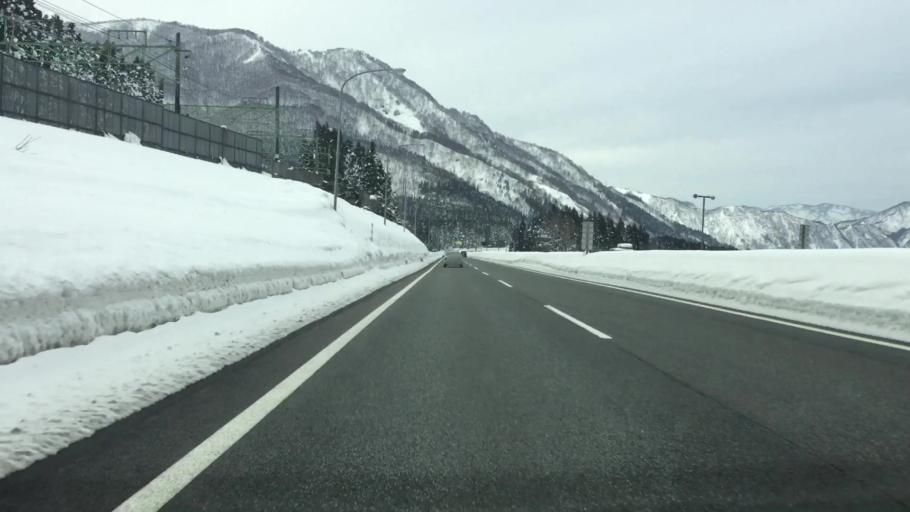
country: JP
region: Niigata
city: Shiozawa
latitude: 36.8769
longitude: 138.8601
